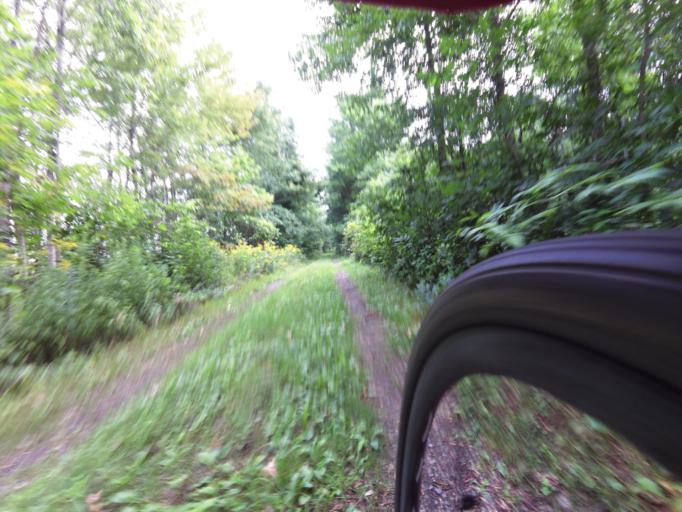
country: CA
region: Ontario
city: Perth
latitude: 44.6434
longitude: -76.2316
